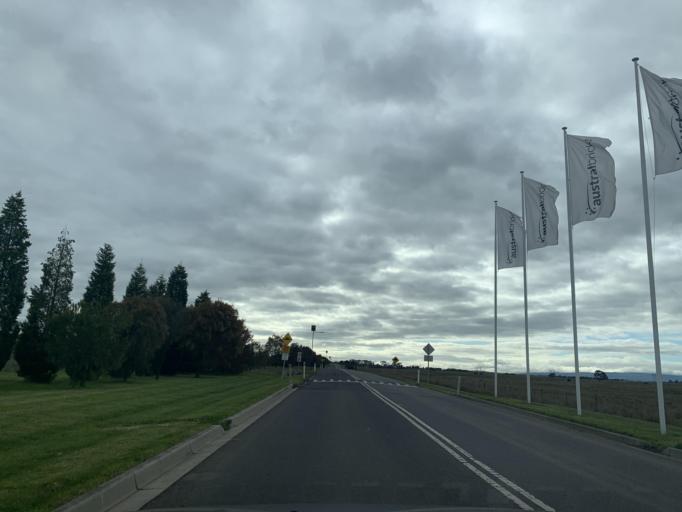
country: AU
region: Victoria
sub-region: Hume
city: Craigieburn
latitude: -37.6018
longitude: 144.9727
